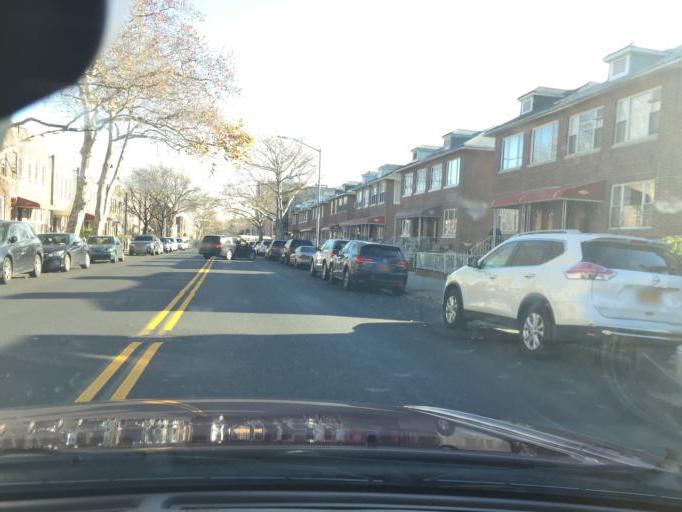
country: US
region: New York
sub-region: Kings County
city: Bensonhurst
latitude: 40.6189
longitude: -73.9820
